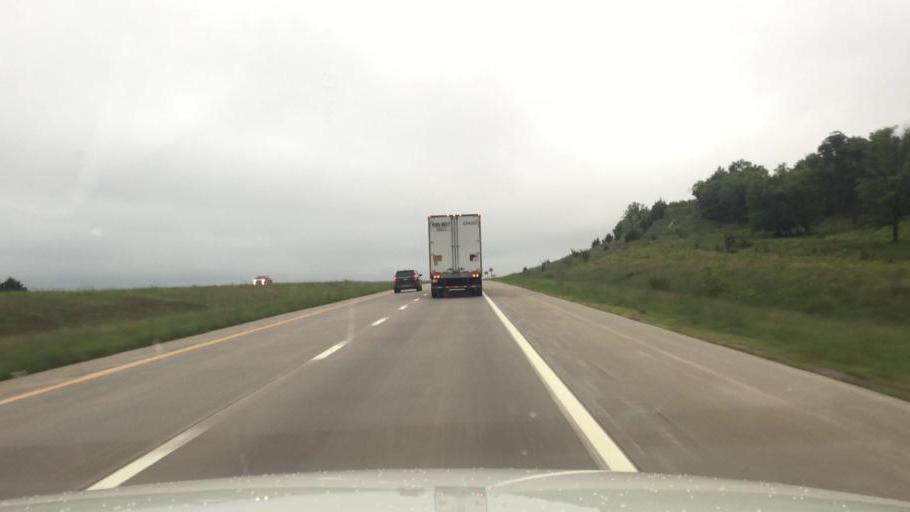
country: US
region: Kansas
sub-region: Montgomery County
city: Cherryvale
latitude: 37.2153
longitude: -95.5854
